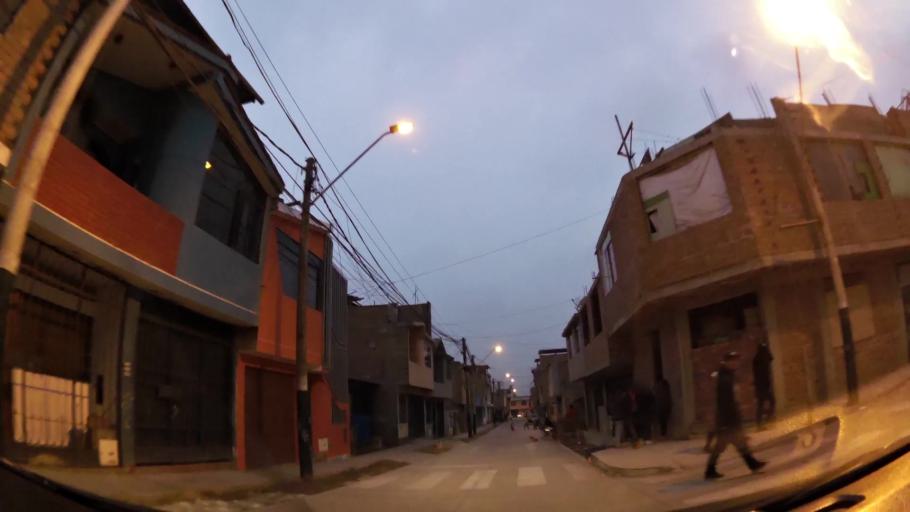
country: PE
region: Lima
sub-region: Lima
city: Surco
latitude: -12.1893
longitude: -76.9754
